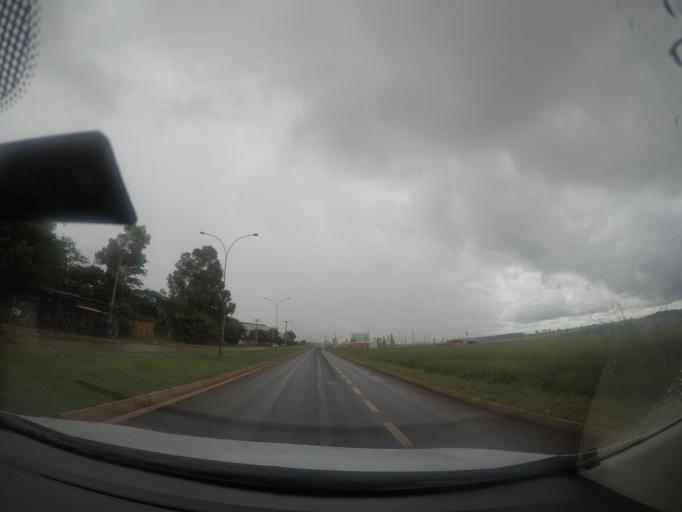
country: BR
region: Goias
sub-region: Trindade
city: Trindade
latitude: -16.6337
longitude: -49.4150
